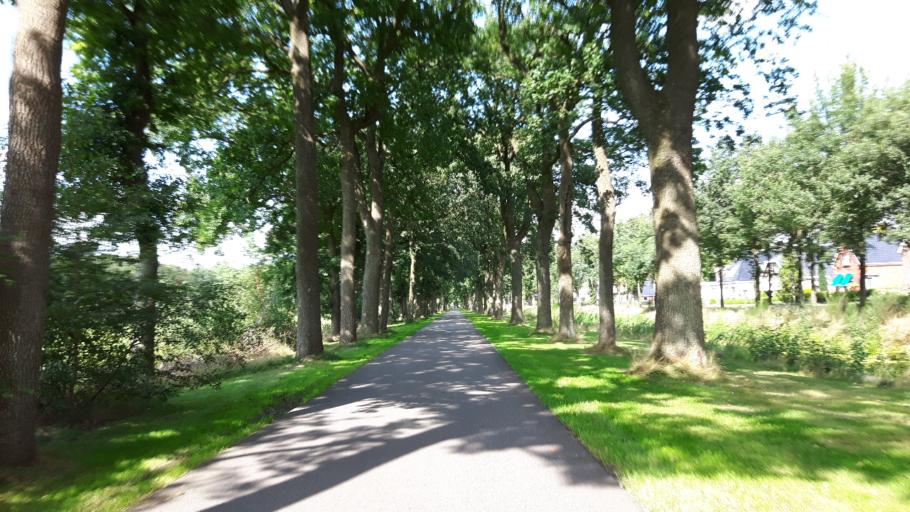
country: NL
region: Friesland
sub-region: Gemeente Smallingerland
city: Drachtstercompagnie
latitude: 53.0766
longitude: 6.2610
